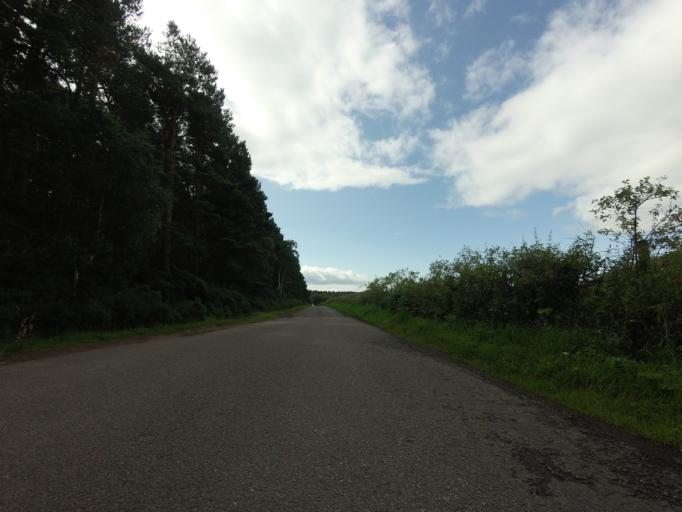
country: GB
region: Scotland
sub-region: Highland
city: Nairn
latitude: 57.5649
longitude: -3.8668
